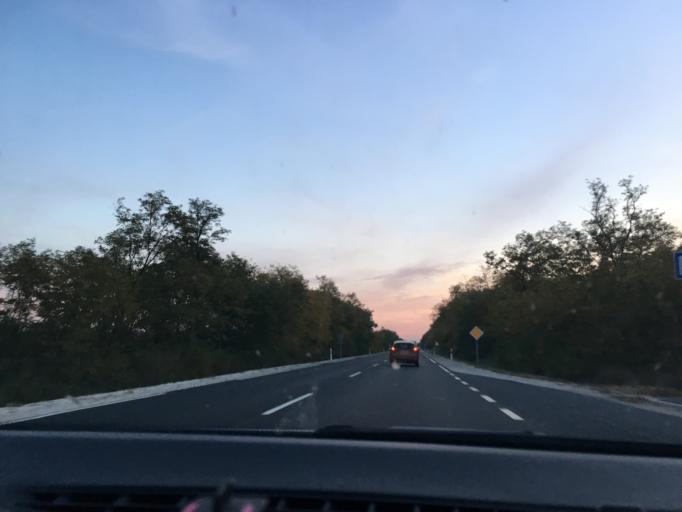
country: HU
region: Hajdu-Bihar
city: Hajduhadhaz
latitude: 47.6167
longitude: 21.6585
